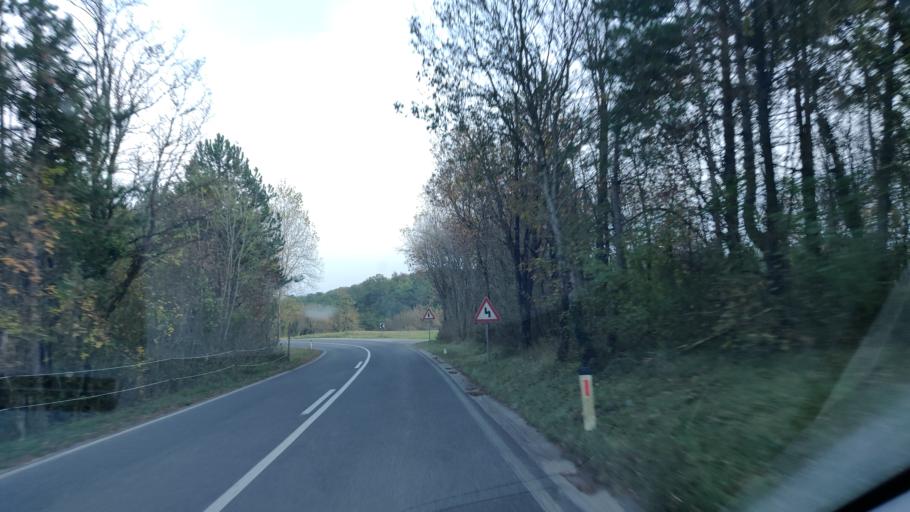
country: SI
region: Komen
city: Komen
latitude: 45.8201
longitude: 13.7555
